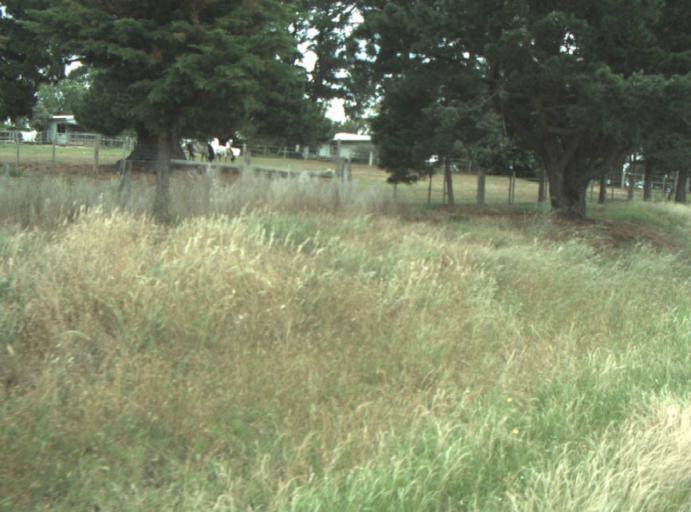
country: AU
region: Victoria
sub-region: Greater Geelong
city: Leopold
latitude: -38.1969
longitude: 144.5099
